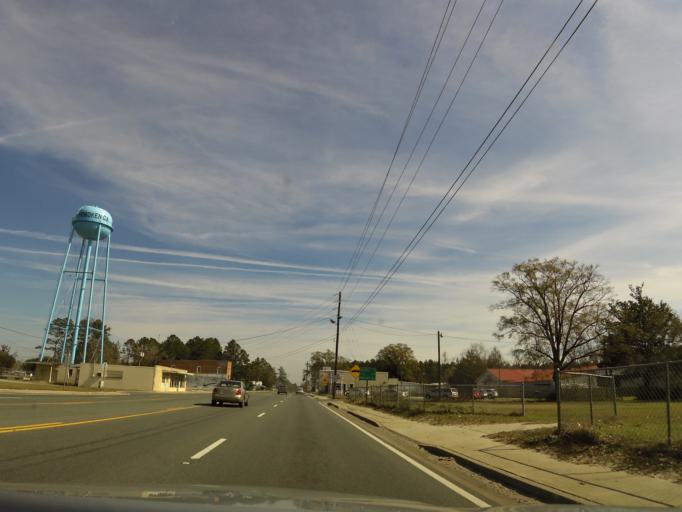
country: US
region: Georgia
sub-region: Brantley County
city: Nahunta
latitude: 31.1811
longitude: -82.1339
